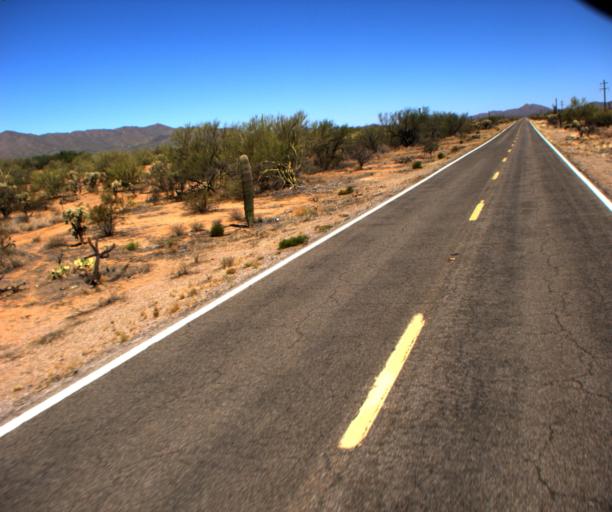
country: US
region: Arizona
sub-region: Pima County
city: Sells
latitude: 32.1065
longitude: -112.0706
